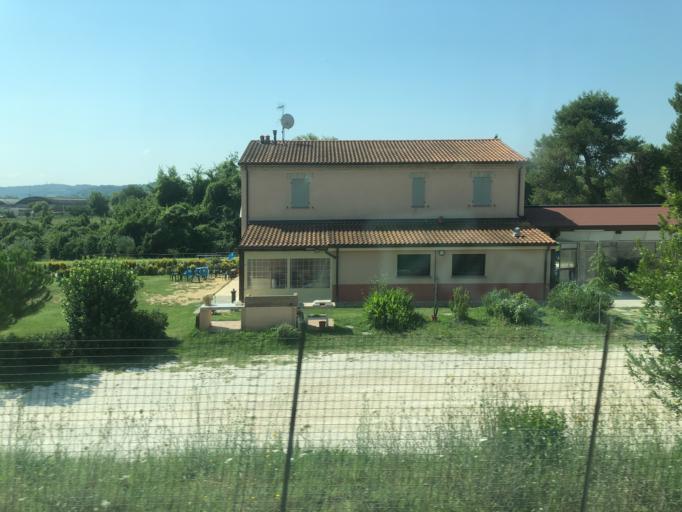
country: IT
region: The Marches
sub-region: Provincia di Pesaro e Urbino
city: Pesaro
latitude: 43.9097
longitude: 12.8831
